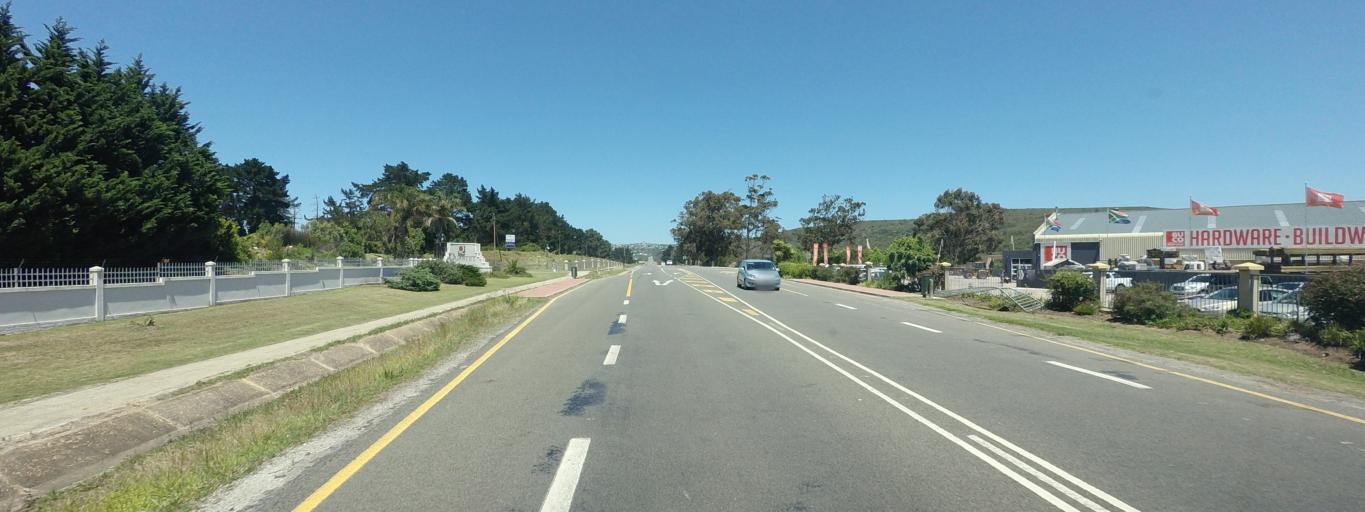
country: ZA
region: Western Cape
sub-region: Eden District Municipality
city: Plettenberg Bay
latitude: -34.0218
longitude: 23.3821
